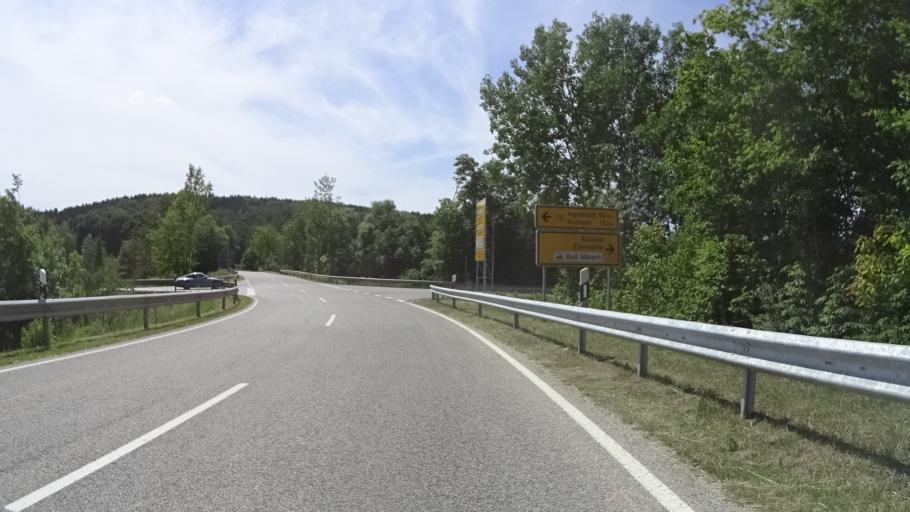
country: DE
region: Bavaria
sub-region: Lower Bavaria
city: Teugn
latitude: 48.9257
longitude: 12.0135
